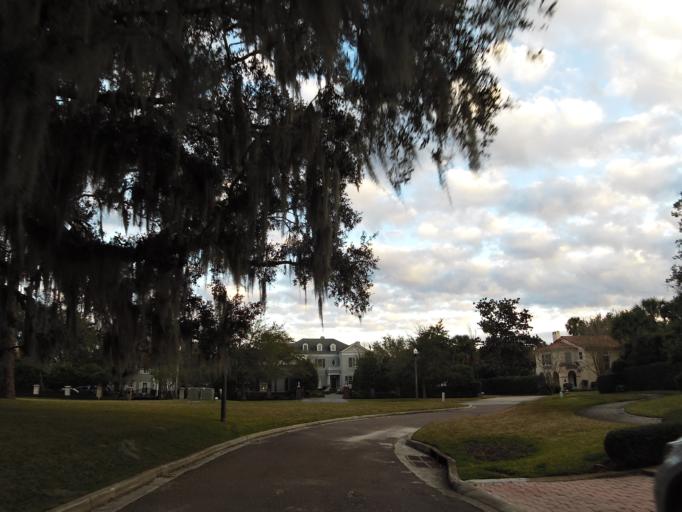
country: US
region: Florida
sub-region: Duval County
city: Jacksonville
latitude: 30.2990
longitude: -81.6996
